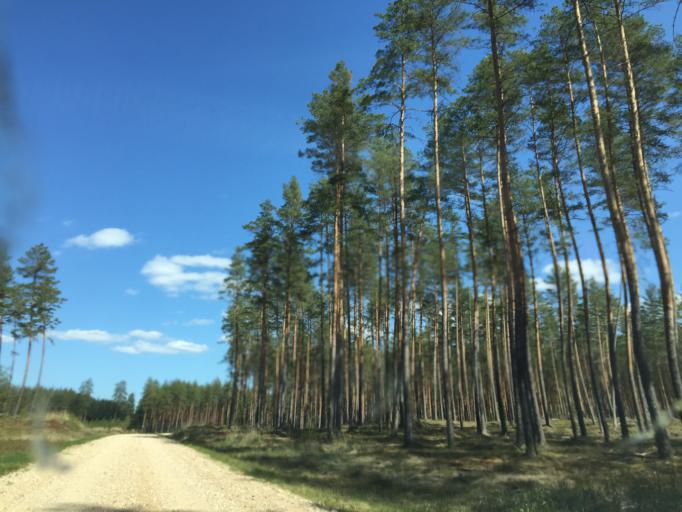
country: LV
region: Vecumnieki
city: Vecumnieki
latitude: 56.6577
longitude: 24.4846
